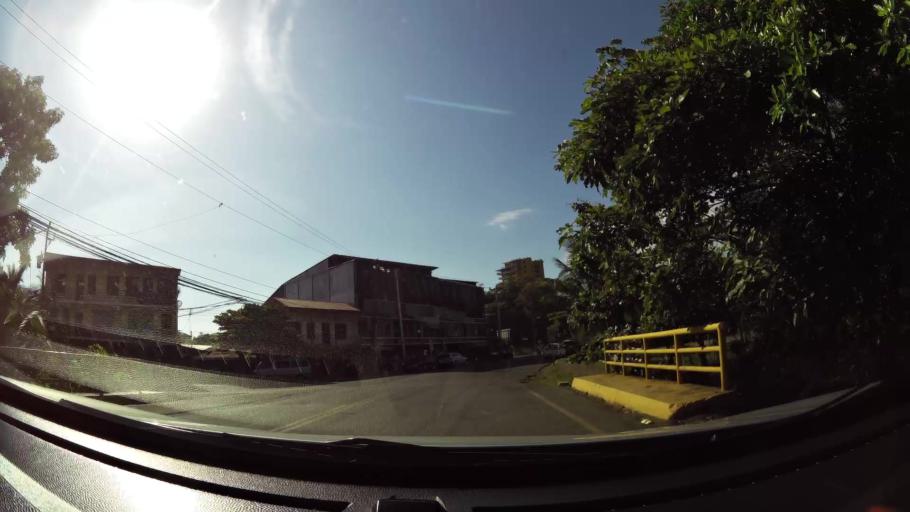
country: CR
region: Puntarenas
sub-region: Canton de Garabito
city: Jaco
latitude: 9.6100
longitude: -84.6239
